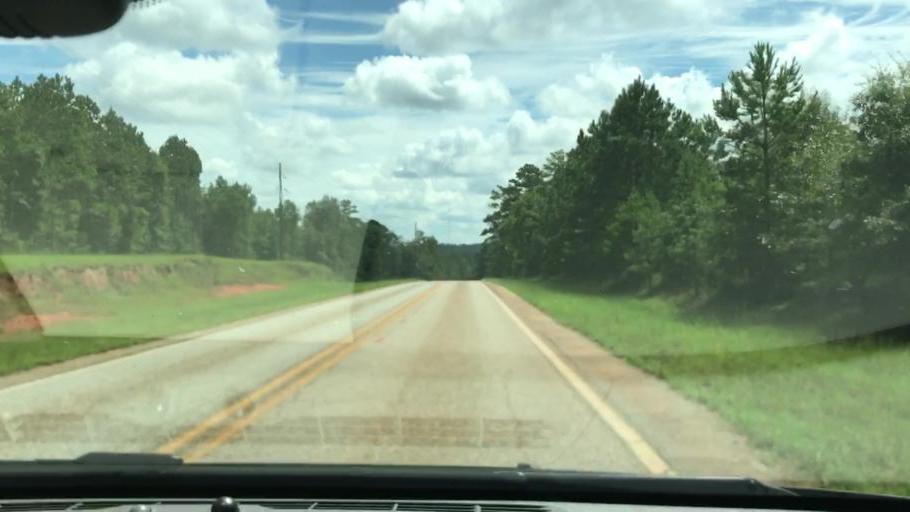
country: US
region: Georgia
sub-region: Stewart County
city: Lumpkin
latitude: 32.0616
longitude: -84.8277
